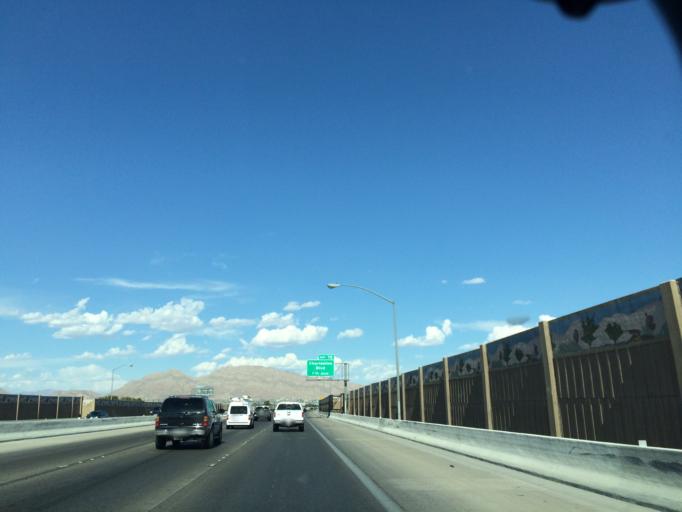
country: US
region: Nevada
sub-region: Clark County
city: Las Vegas
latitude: 36.1678
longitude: -115.1177
